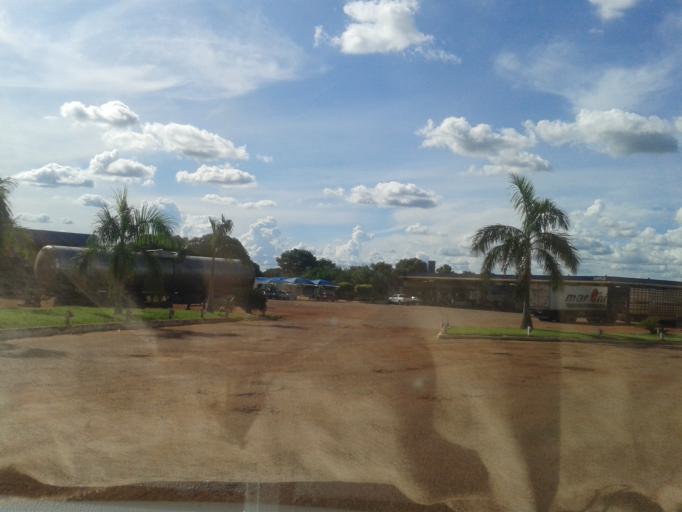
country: BR
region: Goias
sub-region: Mozarlandia
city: Mozarlandia
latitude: -14.7561
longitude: -50.5403
